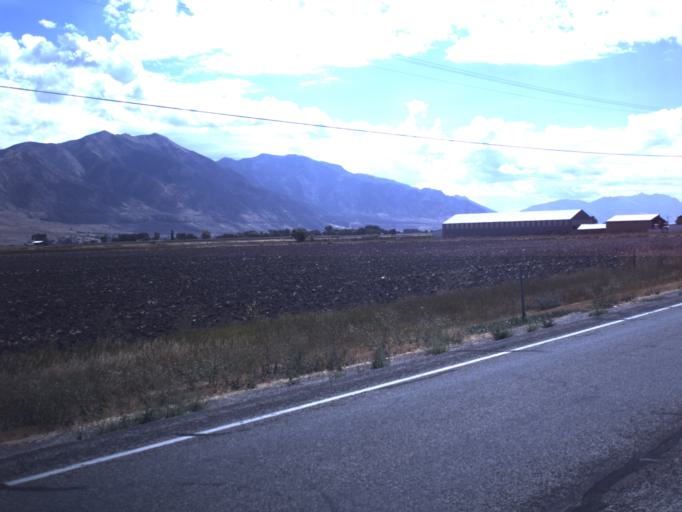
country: US
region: Utah
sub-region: Box Elder County
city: Garland
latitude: 41.7544
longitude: -112.1484
